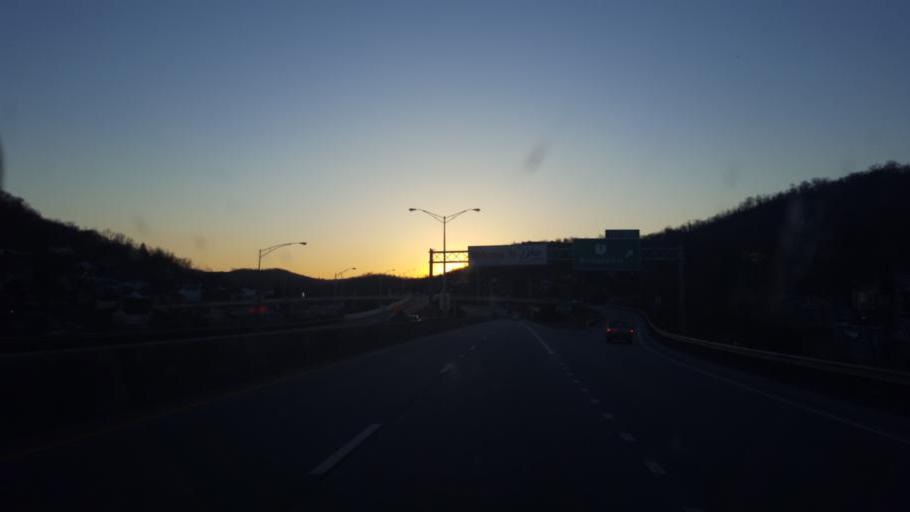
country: US
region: Ohio
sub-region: Belmont County
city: Bridgeport
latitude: 40.0717
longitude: -80.7426
